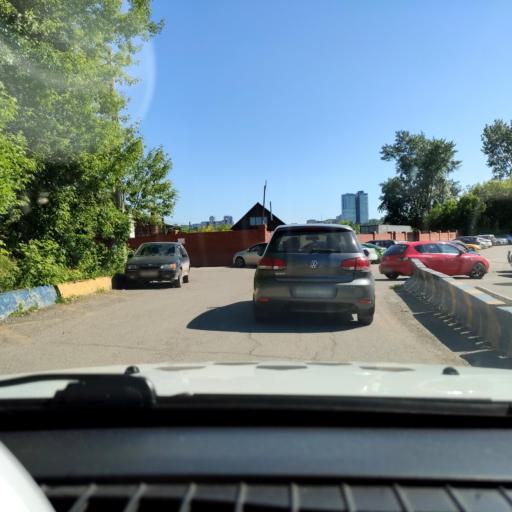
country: RU
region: Perm
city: Perm
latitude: 58.0257
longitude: 56.2234
